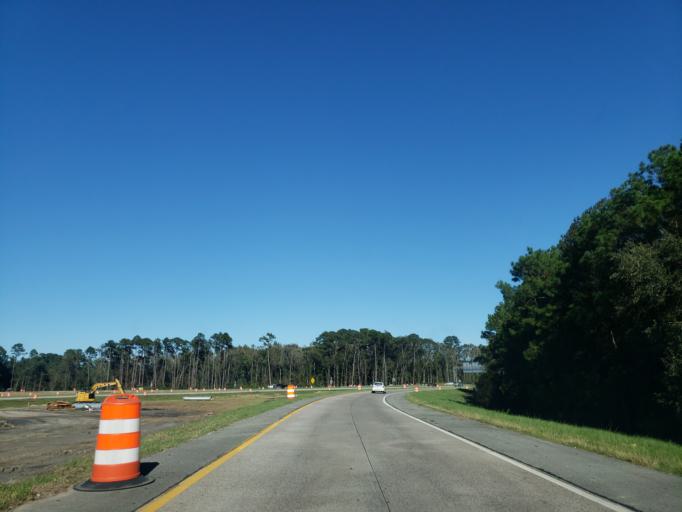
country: US
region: Georgia
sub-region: Chatham County
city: Pooler
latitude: 32.0727
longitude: -81.2447
